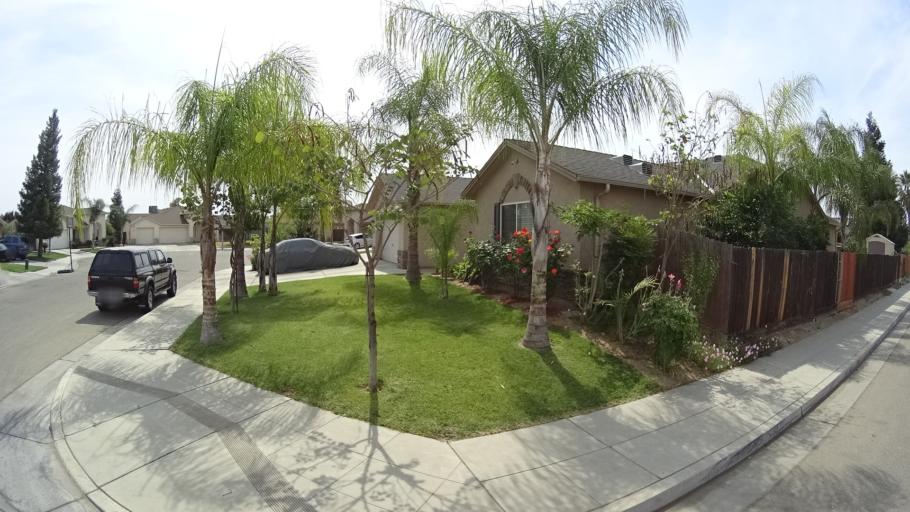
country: US
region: California
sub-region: Fresno County
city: West Park
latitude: 36.7627
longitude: -119.8753
